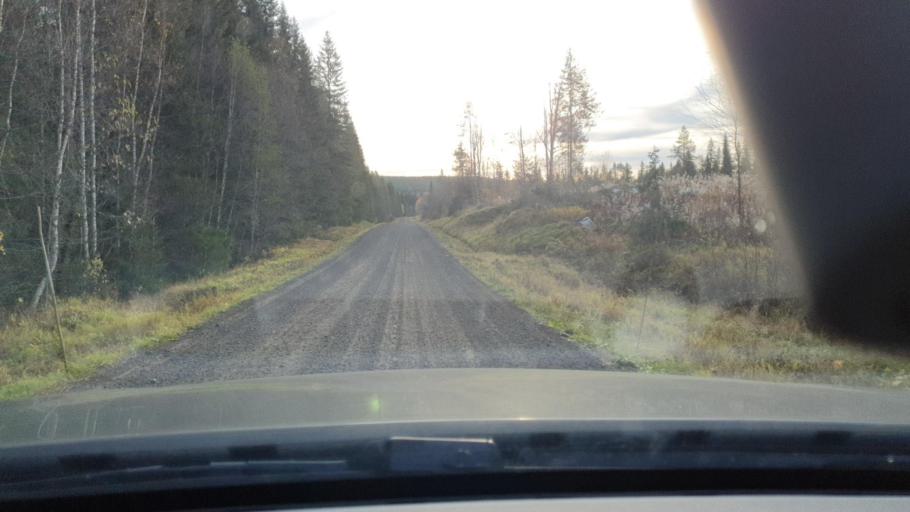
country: SE
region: Jaemtland
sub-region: Stroemsunds Kommun
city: Stroemsund
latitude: 63.5165
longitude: 15.6442
